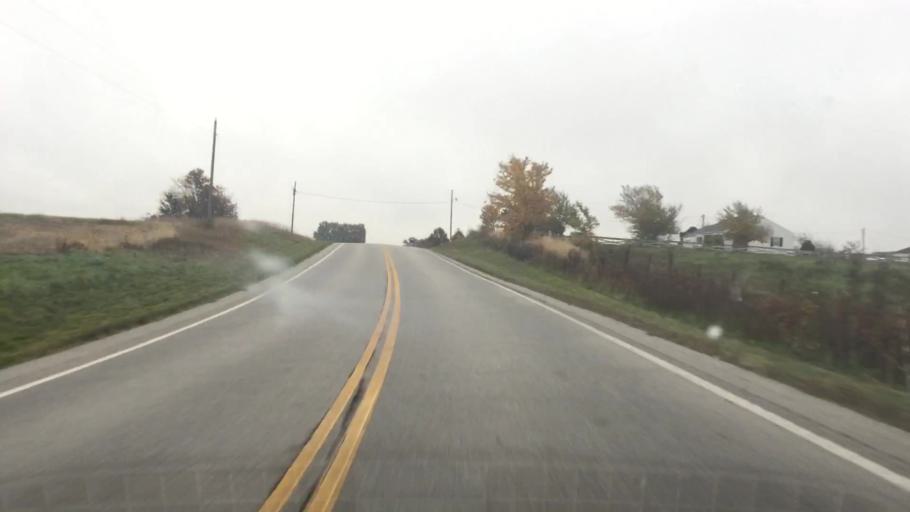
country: US
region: Missouri
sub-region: Boone County
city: Columbia
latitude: 38.9187
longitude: -92.1891
